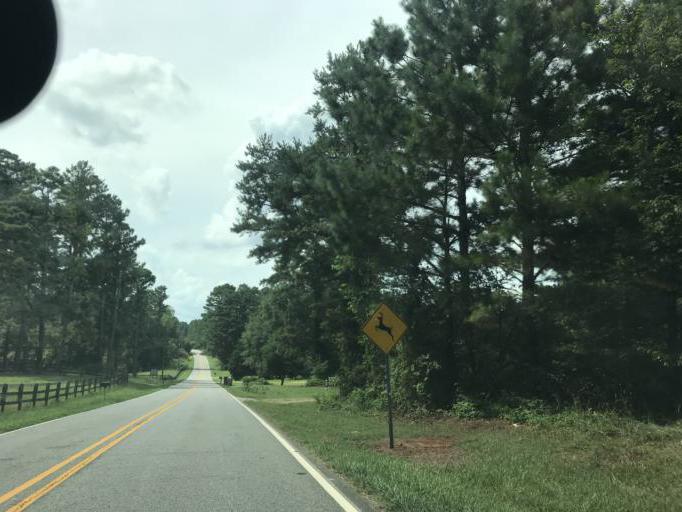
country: US
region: Georgia
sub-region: Forsyth County
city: Cumming
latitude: 34.2187
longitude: -84.2388
